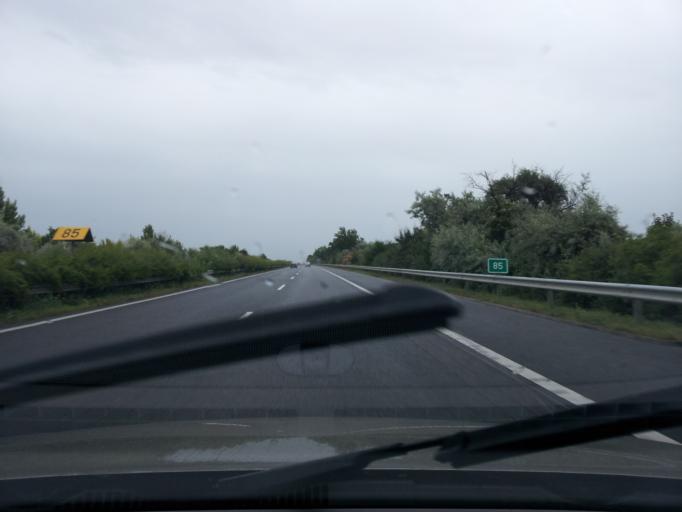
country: HU
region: Fejer
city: Lepseny
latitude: 47.0143
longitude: 18.2436
